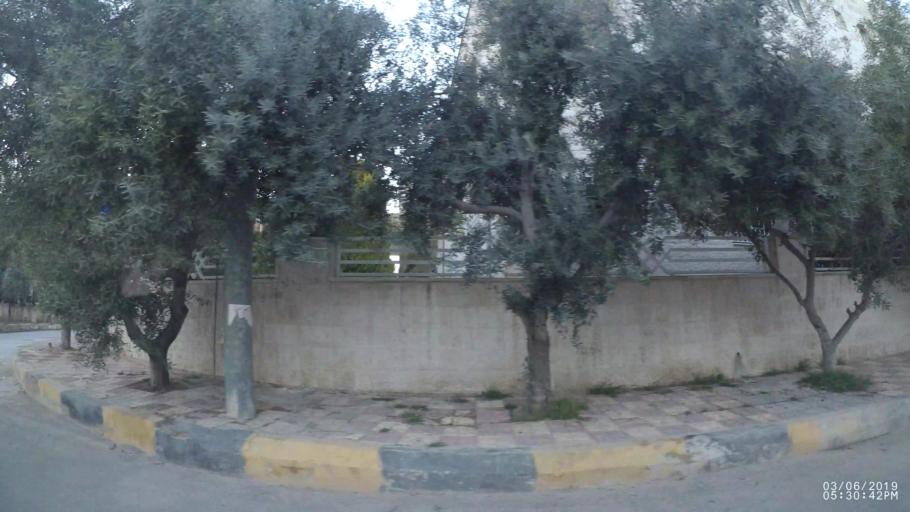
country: JO
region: Amman
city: Amman
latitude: 31.9894
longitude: 35.9656
